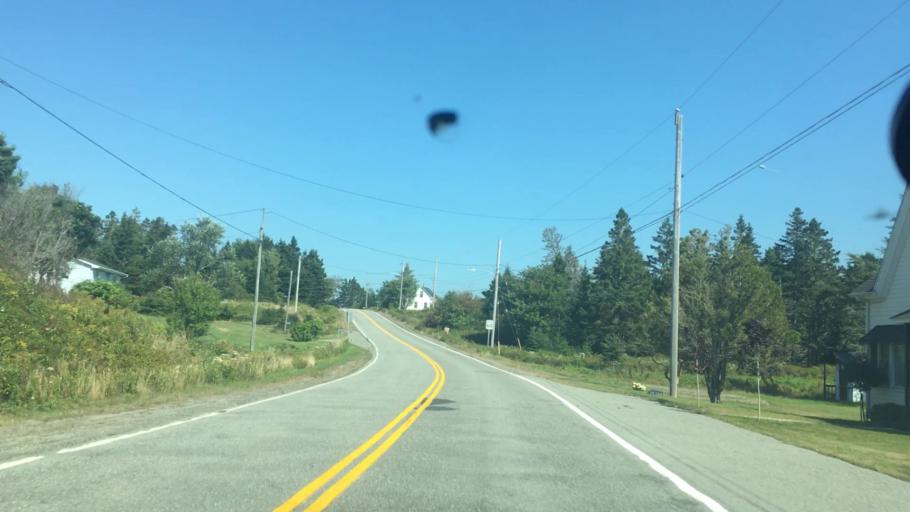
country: CA
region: Nova Scotia
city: New Glasgow
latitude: 44.9117
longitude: -62.3845
